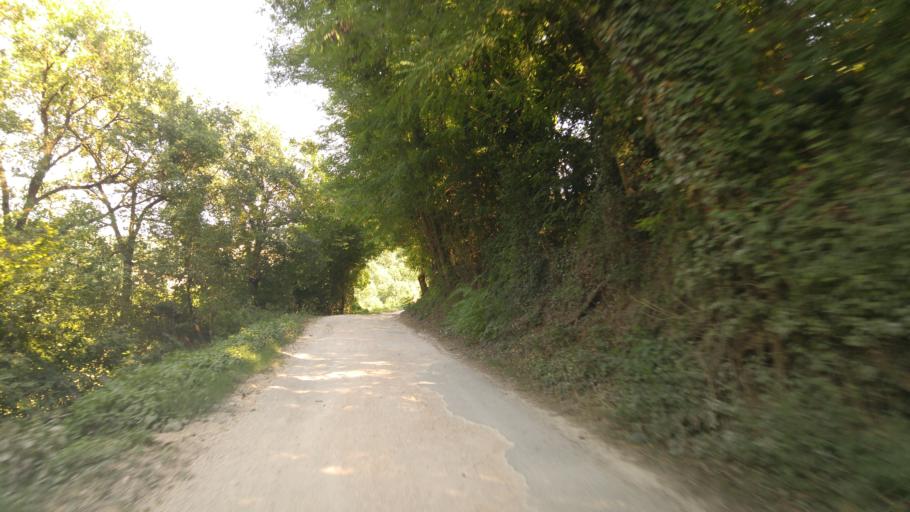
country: IT
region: The Marches
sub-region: Provincia di Pesaro e Urbino
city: Fossombrone
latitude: 43.6798
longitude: 12.7900
